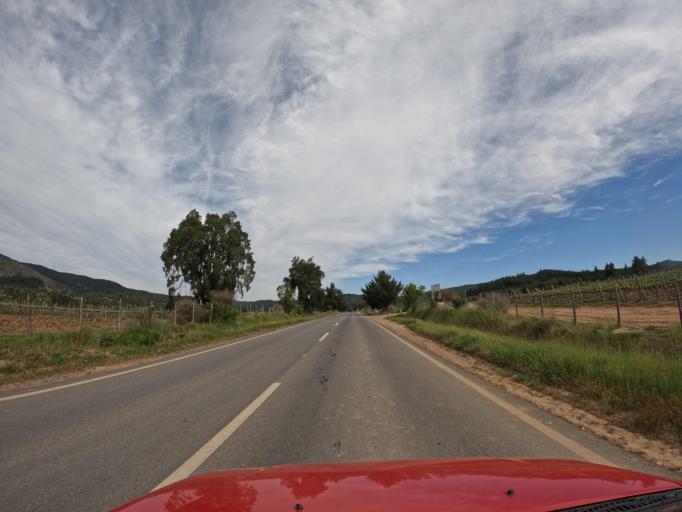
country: CL
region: Maule
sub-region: Provincia de Talca
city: Talca
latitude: -35.3398
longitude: -71.9208
